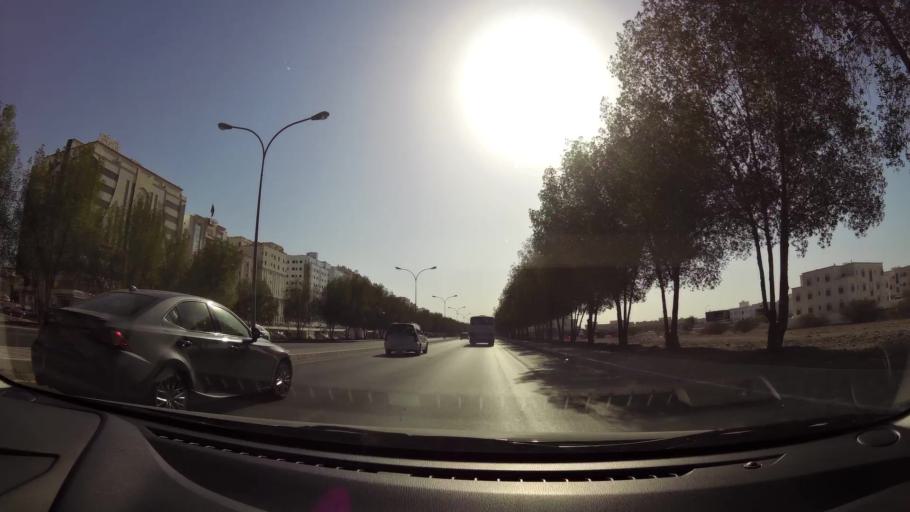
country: OM
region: Muhafazat Masqat
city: As Sib al Jadidah
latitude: 23.6159
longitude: 58.2027
